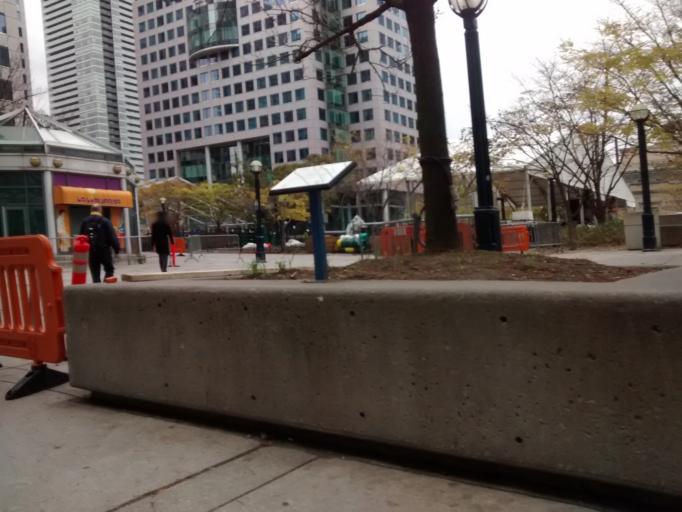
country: CA
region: Ontario
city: Toronto
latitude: 43.6460
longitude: -79.3865
